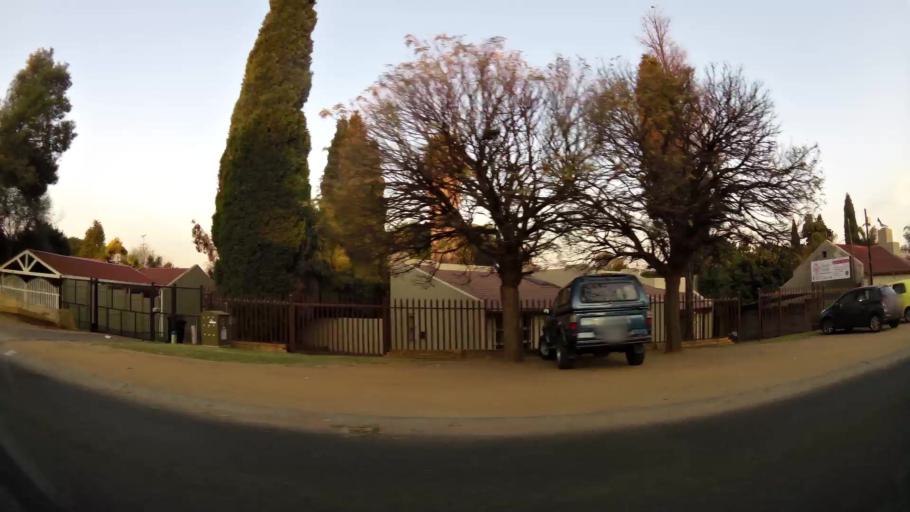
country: ZA
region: Gauteng
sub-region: City of Johannesburg Metropolitan Municipality
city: Modderfontein
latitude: -26.0795
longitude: 28.2213
